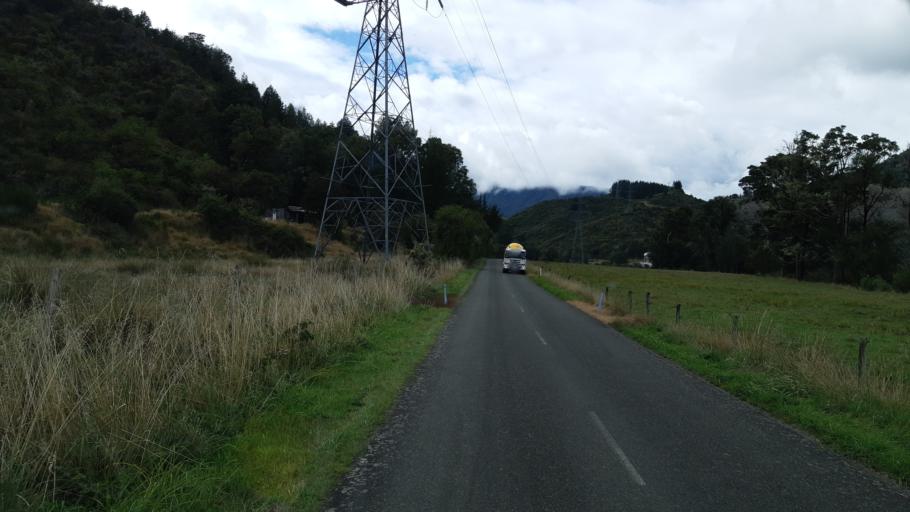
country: NZ
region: West Coast
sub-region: Buller District
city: Westport
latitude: -41.7879
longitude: 172.3564
